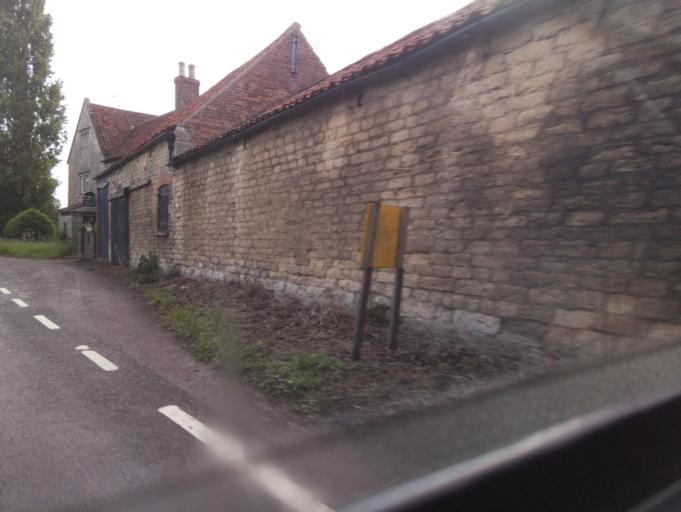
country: GB
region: England
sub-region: Lincolnshire
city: Great Gonerby
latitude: 53.0329
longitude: -0.6526
